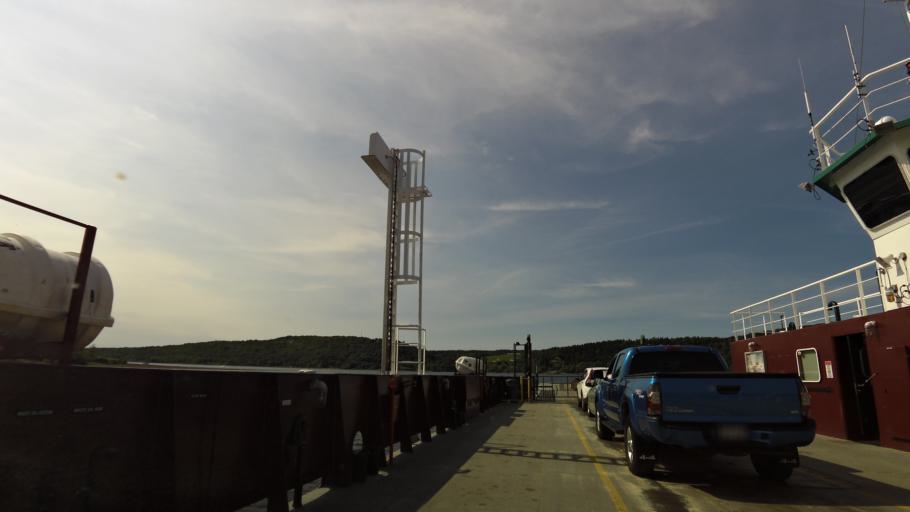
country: CA
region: New Brunswick
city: Hampton
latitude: 45.6108
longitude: -65.9024
